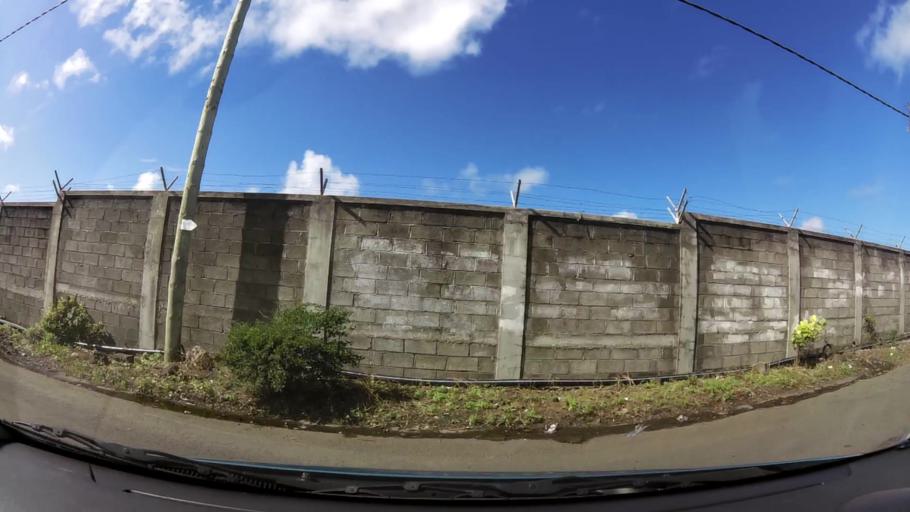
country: MU
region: Grand Port
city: Plaine Magnien
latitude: -20.4281
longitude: 57.6717
